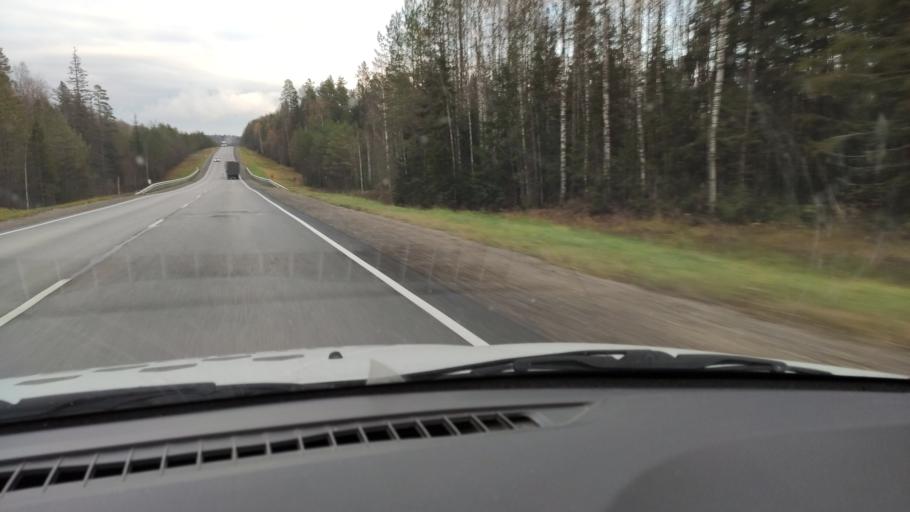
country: RU
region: Kirov
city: Chernaya Kholunitsa
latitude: 58.8261
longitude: 51.7829
